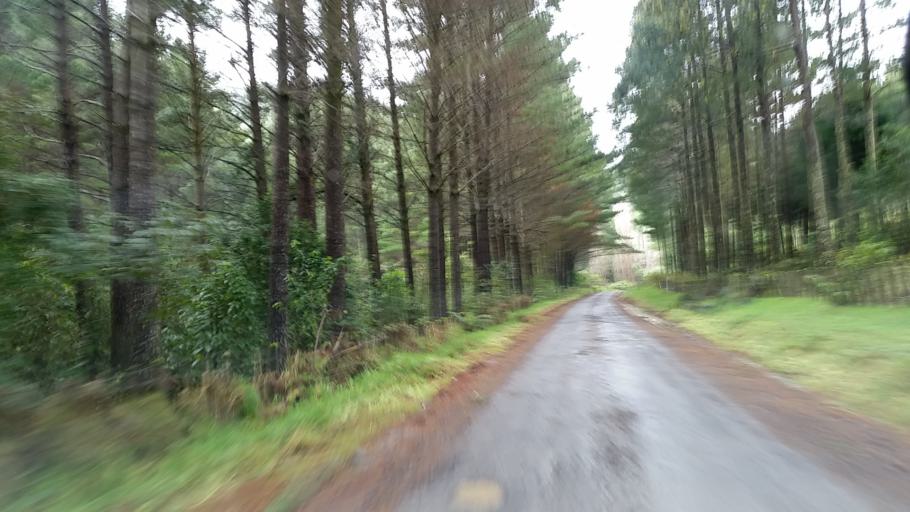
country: NZ
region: Taranaki
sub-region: South Taranaki District
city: Eltham
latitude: -39.5145
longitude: 174.4419
